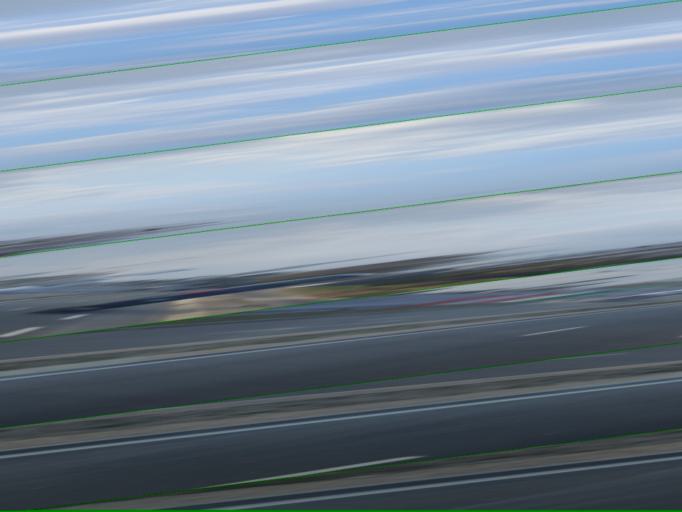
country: FR
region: Ile-de-France
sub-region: Departement des Yvelines
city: Plaisir
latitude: 48.8146
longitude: 1.9595
